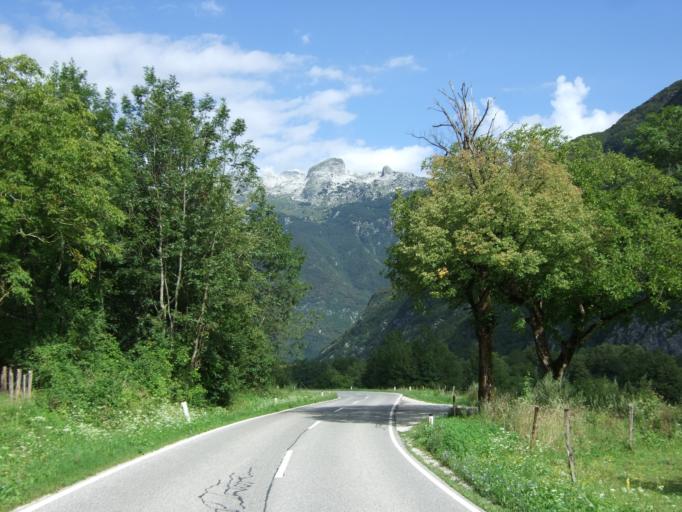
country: SI
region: Bovec
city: Bovec
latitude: 46.2850
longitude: 13.5126
